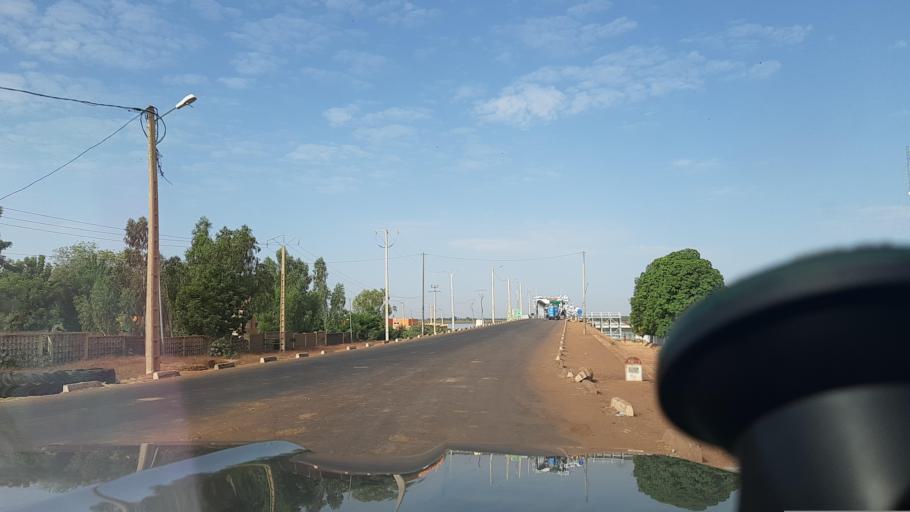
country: ML
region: Segou
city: Markala
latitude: 13.6784
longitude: -6.0758
